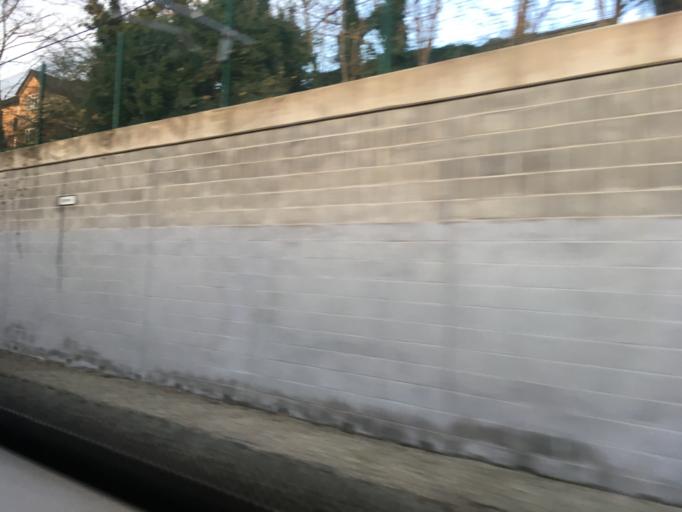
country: GB
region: England
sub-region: Manchester
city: Didsbury
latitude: 53.4181
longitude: -2.2304
